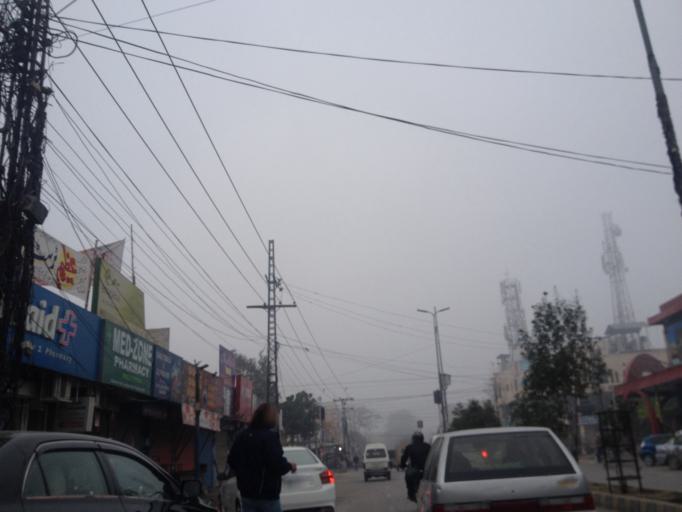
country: PK
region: Punjab
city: Lahore
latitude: 31.4586
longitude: 74.3029
